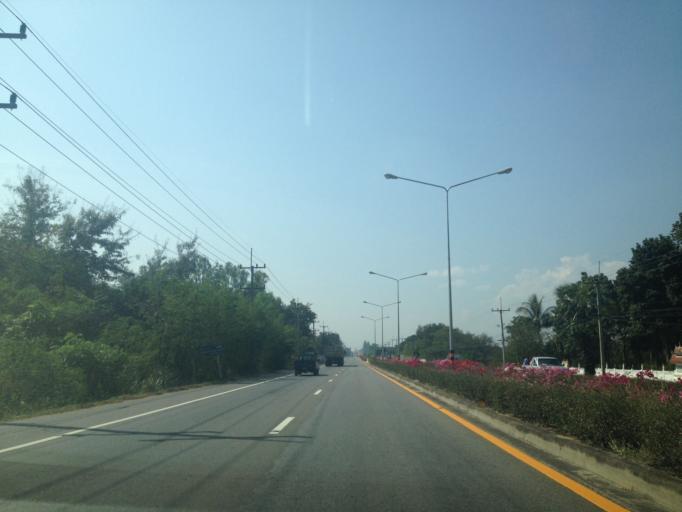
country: TH
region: Chiang Mai
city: Doi Lo
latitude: 18.4813
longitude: 98.8002
